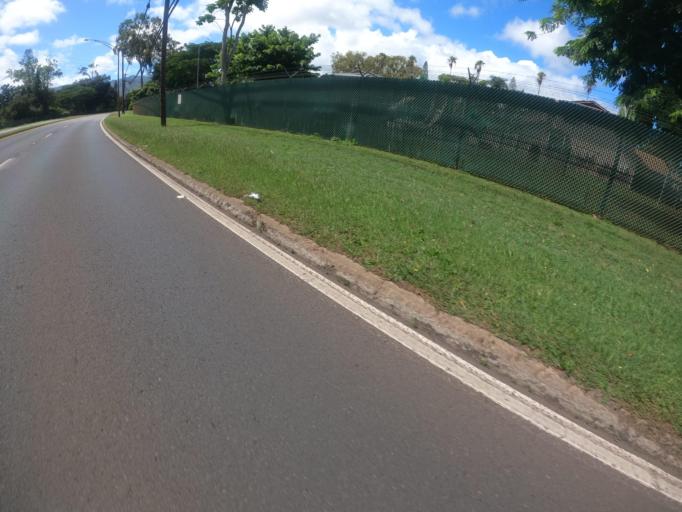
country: US
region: Hawaii
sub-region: Honolulu County
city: Wahiawa
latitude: 21.4860
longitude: -158.0423
